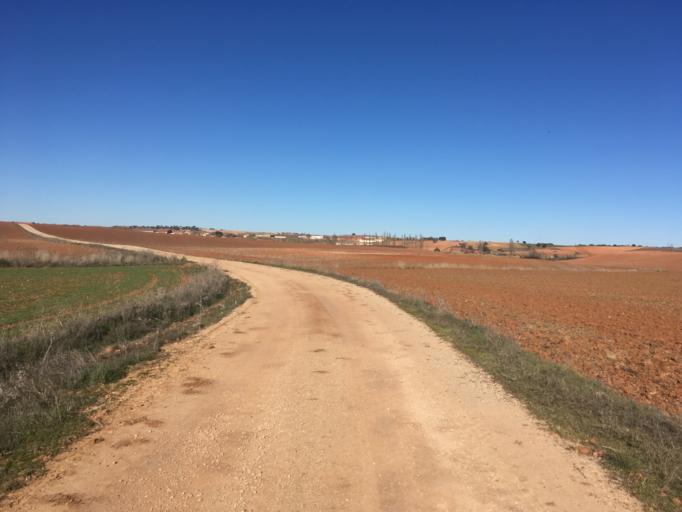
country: ES
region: Castille-La Mancha
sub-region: Provincia de Cuenca
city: Atalaya del Canavate
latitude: 39.5401
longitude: -2.2407
